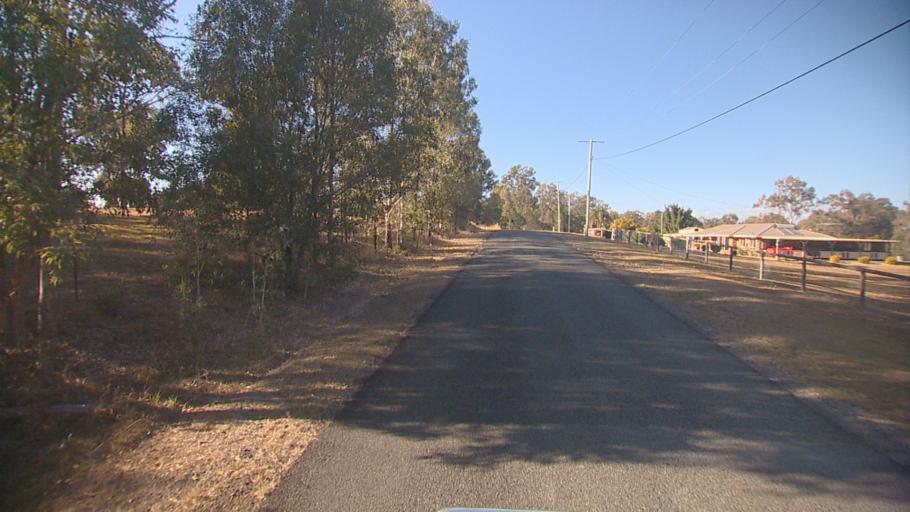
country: AU
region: Queensland
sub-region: Logan
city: Cedar Vale
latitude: -27.8354
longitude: 153.0076
